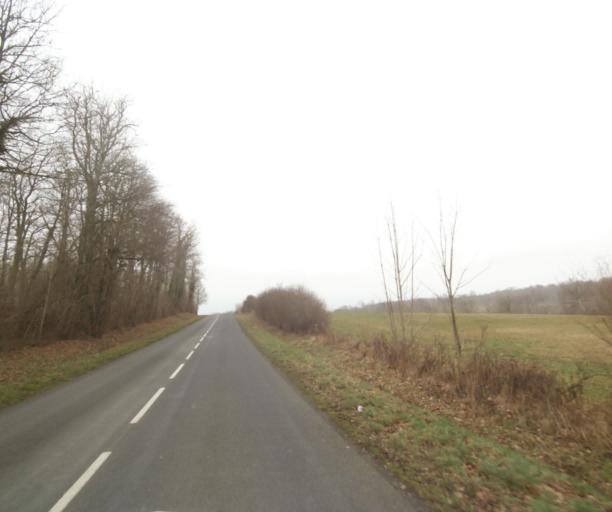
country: FR
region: Champagne-Ardenne
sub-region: Departement de la Marne
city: Pargny-sur-Saulx
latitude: 48.7395
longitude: 4.8707
